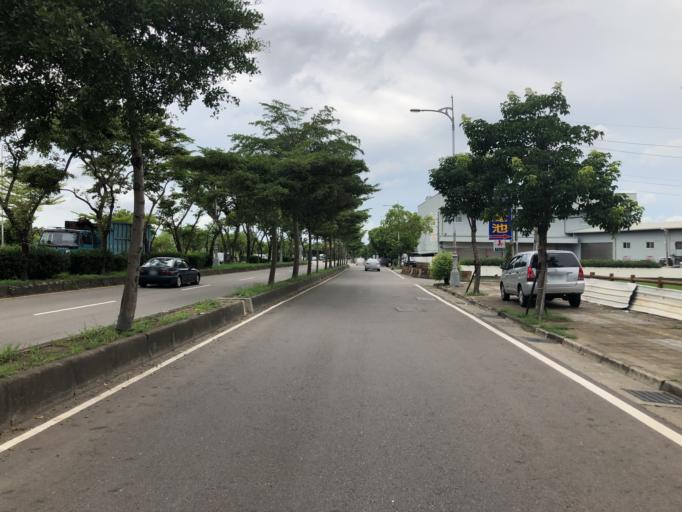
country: TW
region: Taiwan
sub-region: Taichung City
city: Taichung
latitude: 24.0862
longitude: 120.6581
